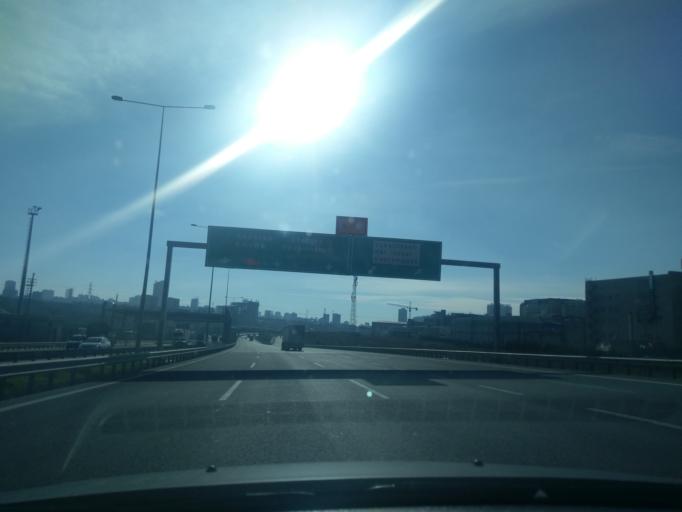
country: TR
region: Istanbul
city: Basaksehir
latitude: 41.0804
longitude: 28.8132
